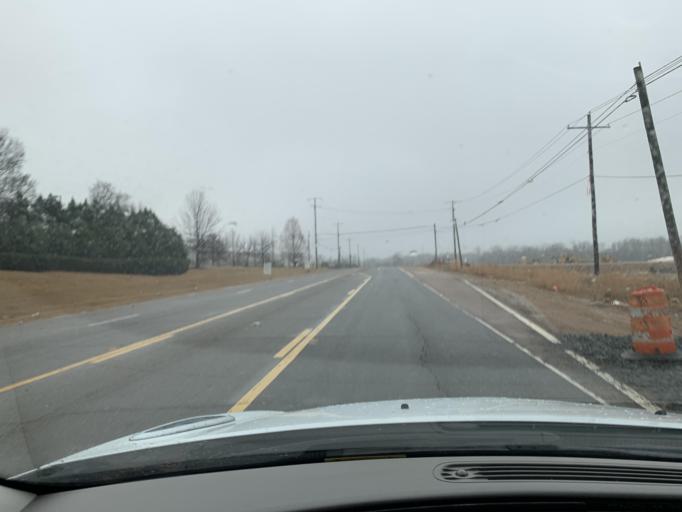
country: US
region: Mississippi
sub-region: De Soto County
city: Horn Lake
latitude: 34.9168
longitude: -90.0052
